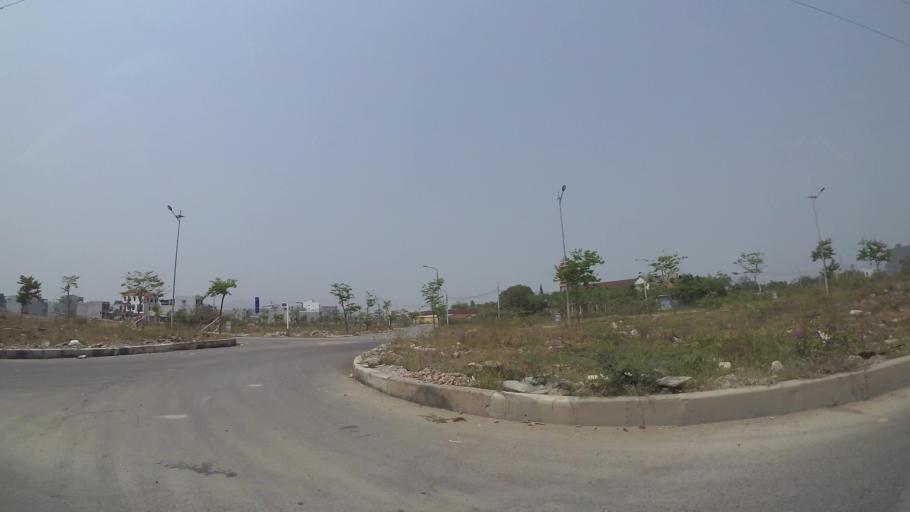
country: VN
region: Da Nang
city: Cam Le
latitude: 16.0139
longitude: 108.2265
